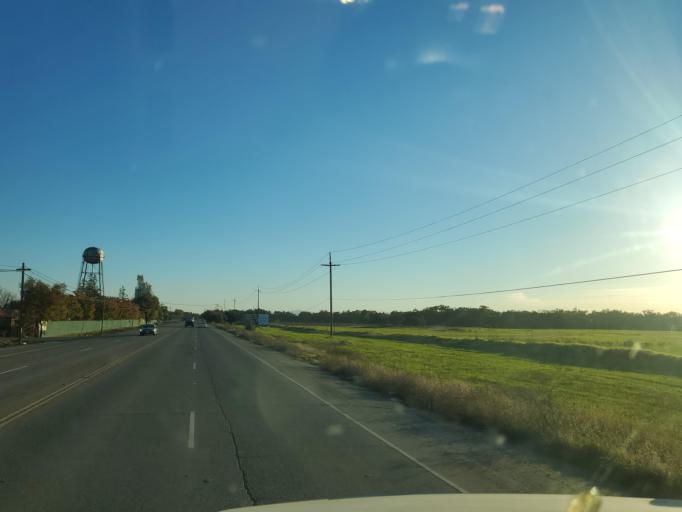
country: US
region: California
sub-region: San Joaquin County
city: Taft Mosswood
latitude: 37.9066
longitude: -121.2757
